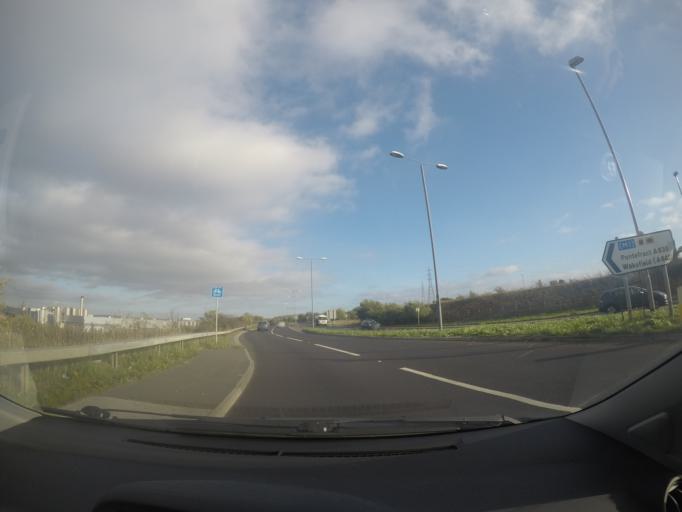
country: GB
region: England
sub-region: City and Borough of Leeds
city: Lofthouse
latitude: 53.7628
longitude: -1.5020
